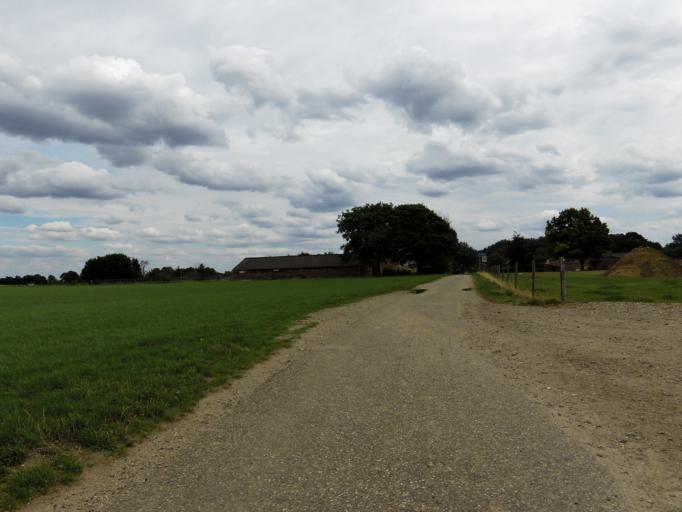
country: NL
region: Limburg
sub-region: Gemeente Schinnen
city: Oirsbeek
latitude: 50.9593
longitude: 5.9205
